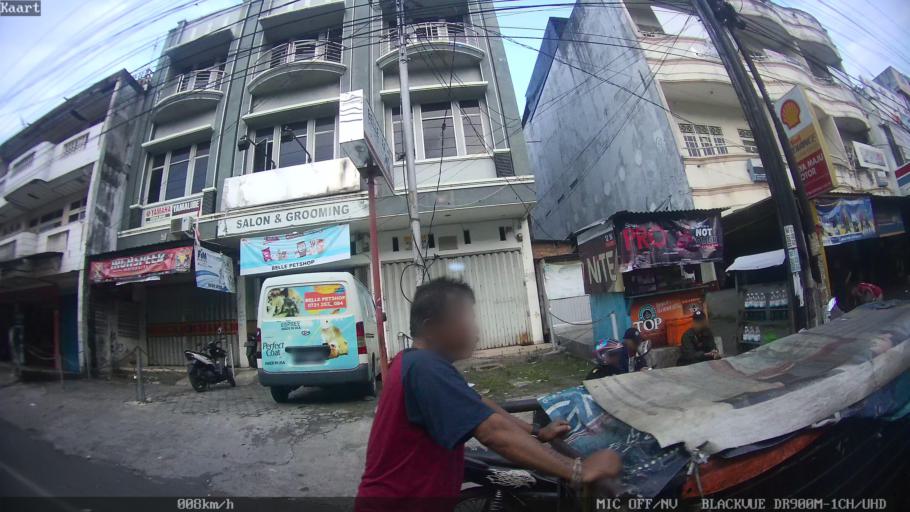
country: ID
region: Lampung
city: Bandarlampung
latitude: -5.4110
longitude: 105.2614
